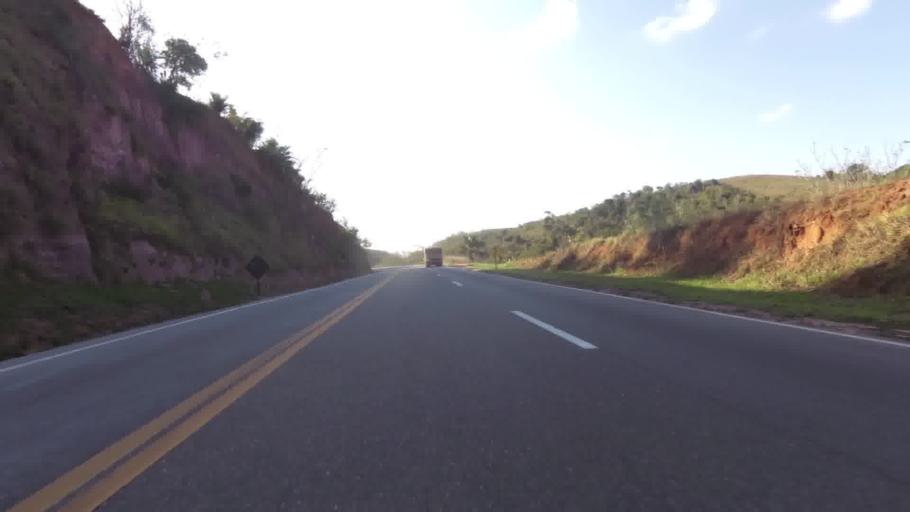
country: BR
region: Espirito Santo
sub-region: Mimoso Do Sul
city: Mimoso do Sul
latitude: -21.2142
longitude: -41.2967
